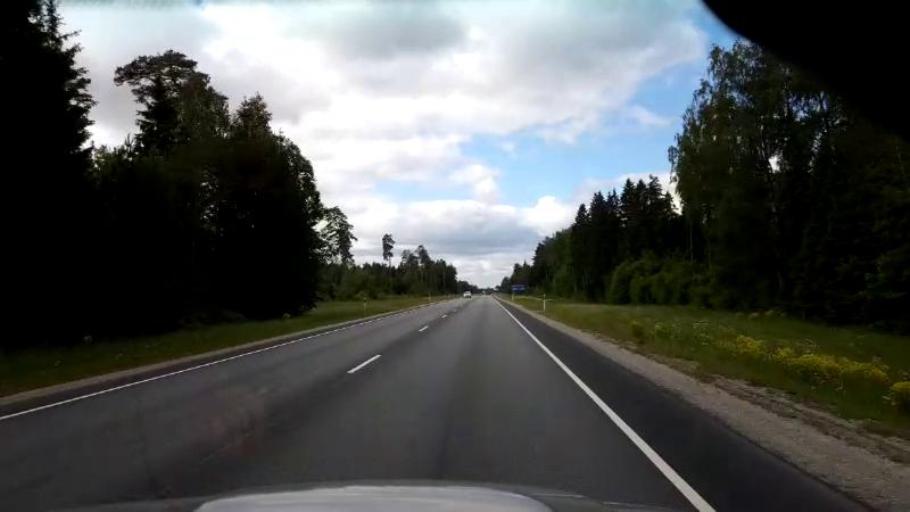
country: EE
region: Harju
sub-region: Nissi vald
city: Riisipere
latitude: 59.0941
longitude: 24.4657
